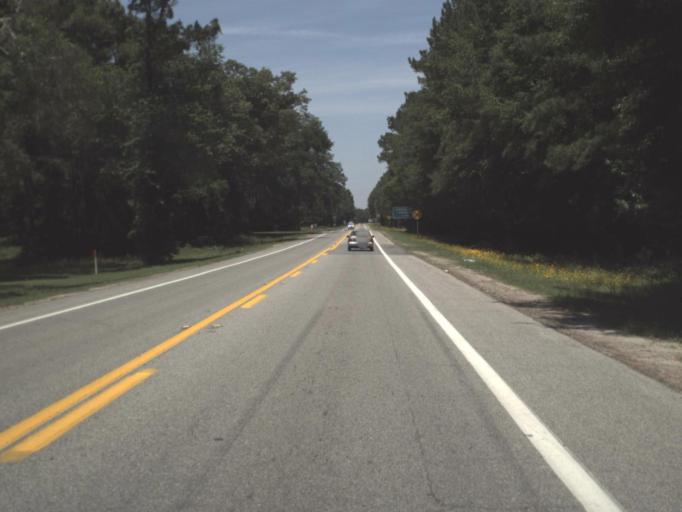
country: US
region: Florida
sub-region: Suwannee County
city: Live Oak
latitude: 30.3741
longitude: -83.1584
